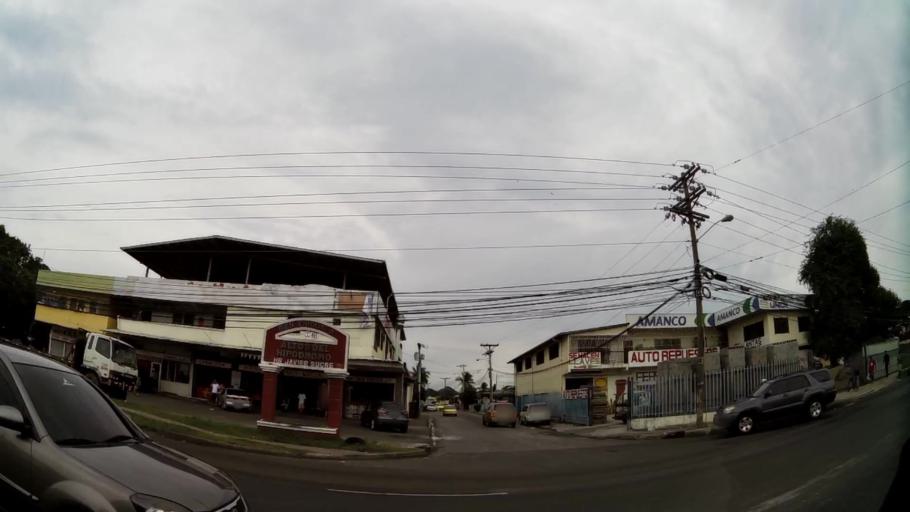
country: PA
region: Panama
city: San Miguelito
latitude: 9.0410
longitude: -79.4586
